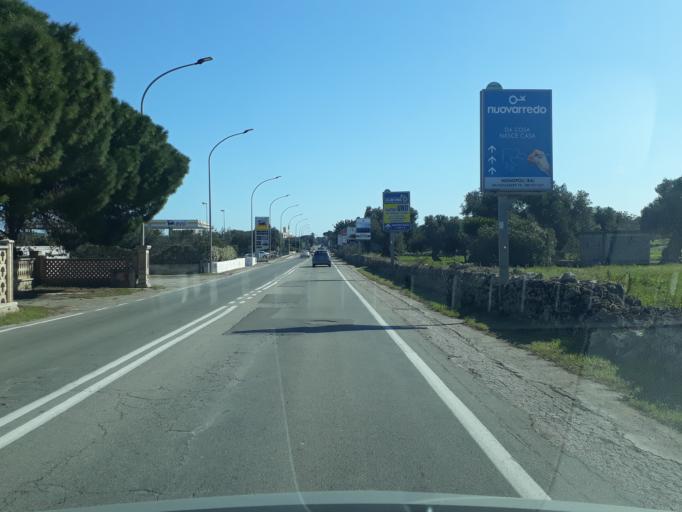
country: IT
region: Apulia
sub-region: Provincia di Bari
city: Monopoli
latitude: 40.9677
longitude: 17.2702
